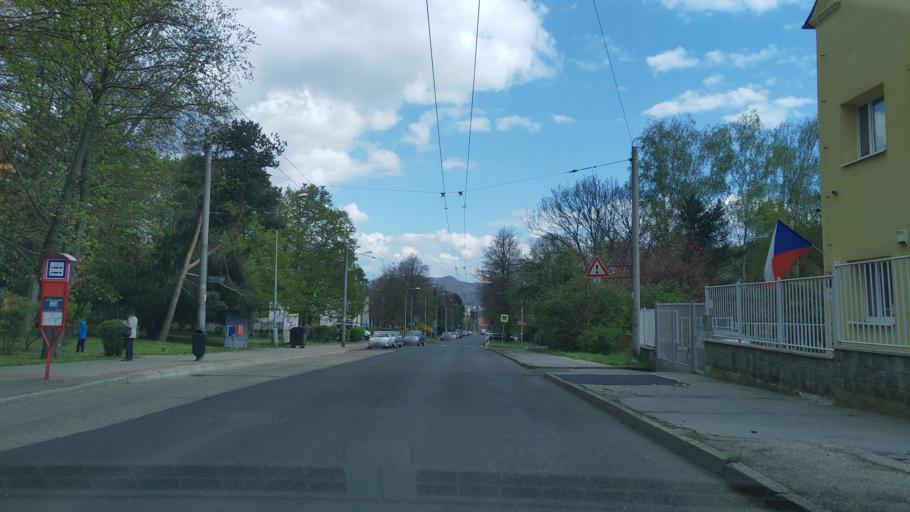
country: CZ
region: Ustecky
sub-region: Okres Usti nad Labem
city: Usti nad Labem
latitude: 50.6847
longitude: 13.9996
